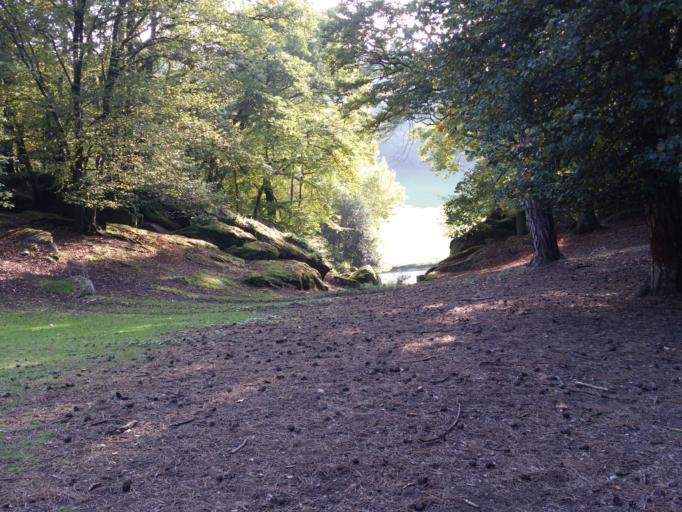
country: FR
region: Ile-de-France
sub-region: Departement des Yvelines
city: Gazeran
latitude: 48.5864
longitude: 1.7529
